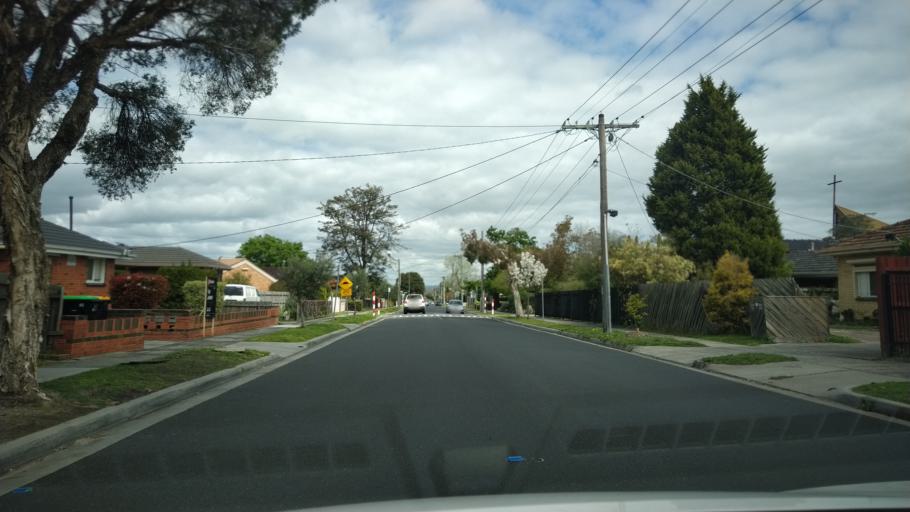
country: AU
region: Victoria
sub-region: Greater Dandenong
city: Noble Park
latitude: -37.9715
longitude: 145.1735
